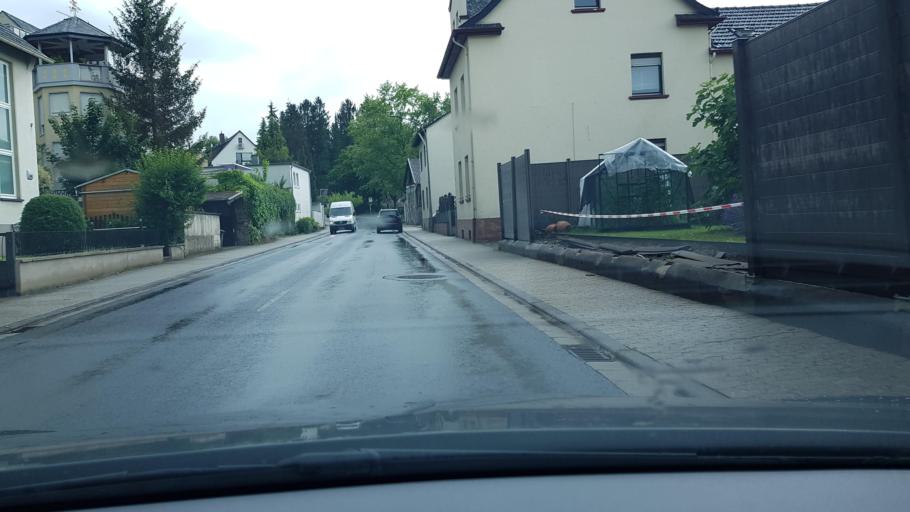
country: DE
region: Rheinland-Pfalz
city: Sinzig
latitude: 50.5421
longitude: 7.2516
